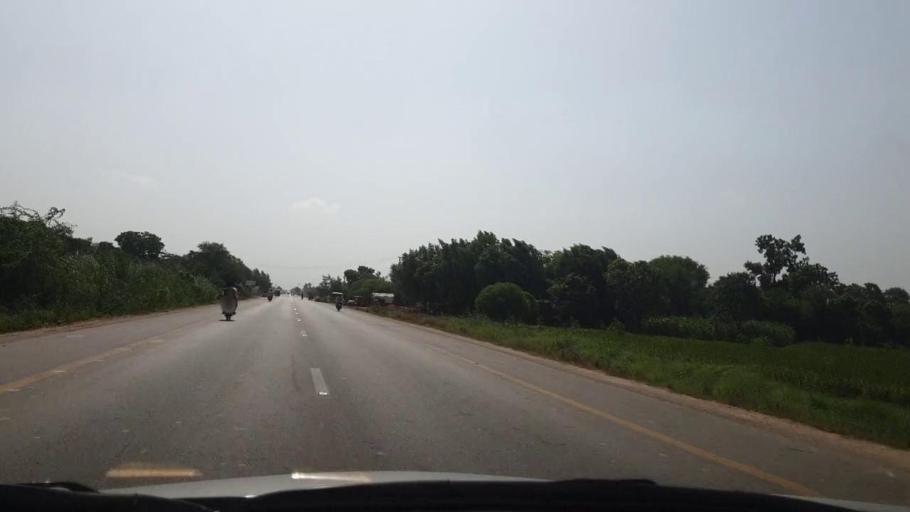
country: PK
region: Sindh
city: Matli
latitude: 25.0655
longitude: 68.6299
